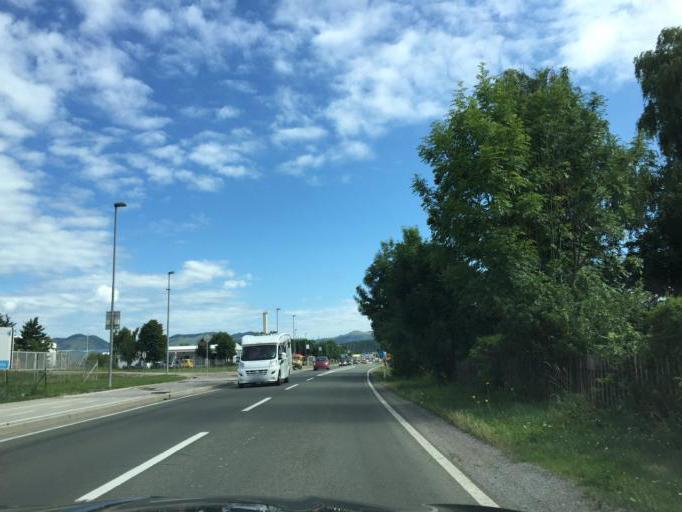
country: SI
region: Postojna
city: Postojna
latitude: 45.7655
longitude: 14.1973
